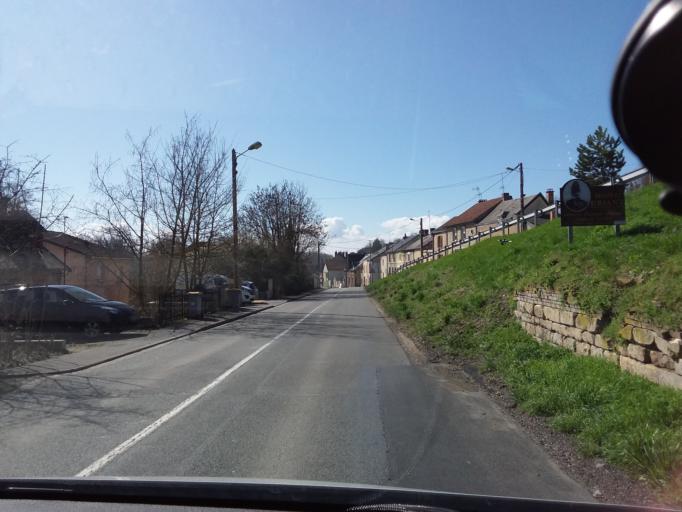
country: FR
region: Picardie
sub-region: Departement de l'Aisne
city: Guignicourt
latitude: 49.4341
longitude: 4.0317
